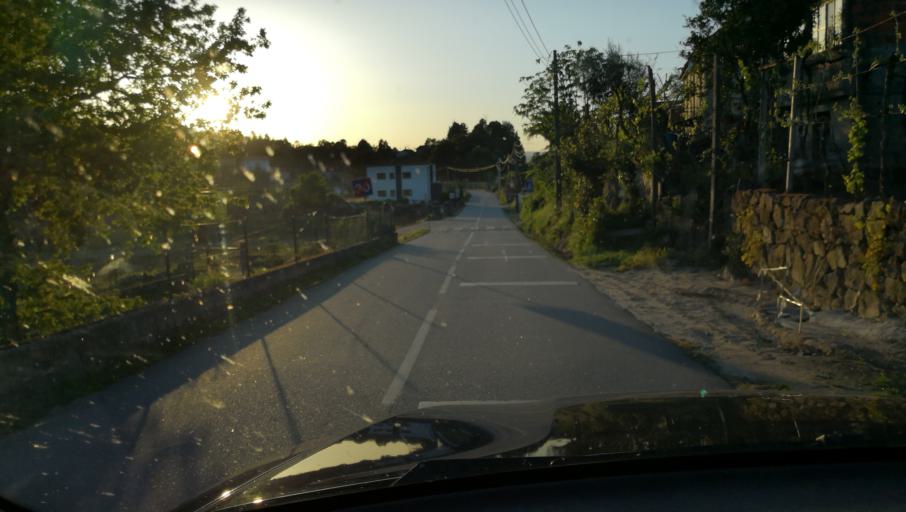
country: PT
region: Vila Real
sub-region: Mondim de Basto
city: Mondim de Basto
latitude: 41.4081
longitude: -7.9272
